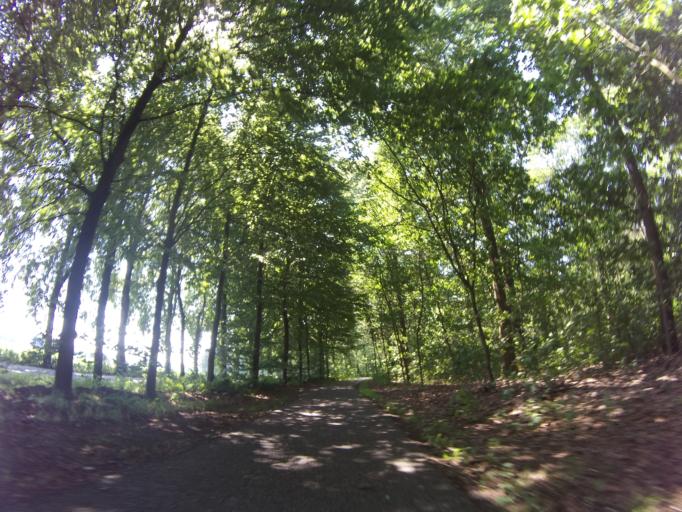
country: NL
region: Drenthe
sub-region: Gemeente Coevorden
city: Sleen
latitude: 52.8033
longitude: 6.8064
